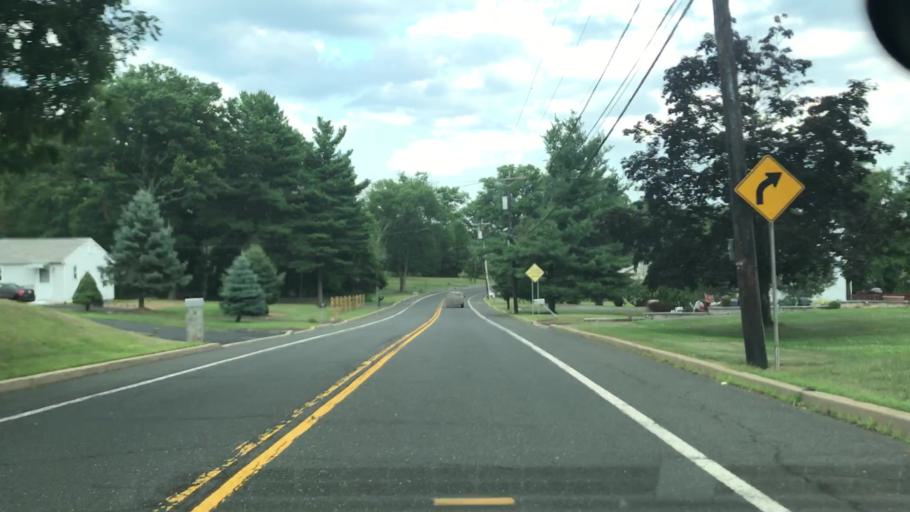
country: US
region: New Jersey
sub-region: Somerset County
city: Bradley Gardens
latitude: 40.5571
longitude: -74.6805
